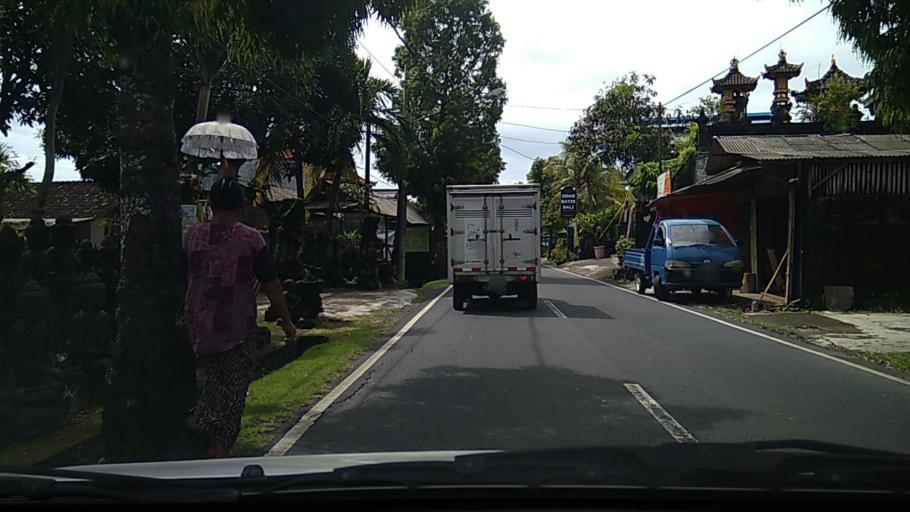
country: ID
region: Bali
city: Banjar Sedang
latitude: -8.5712
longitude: 115.2564
